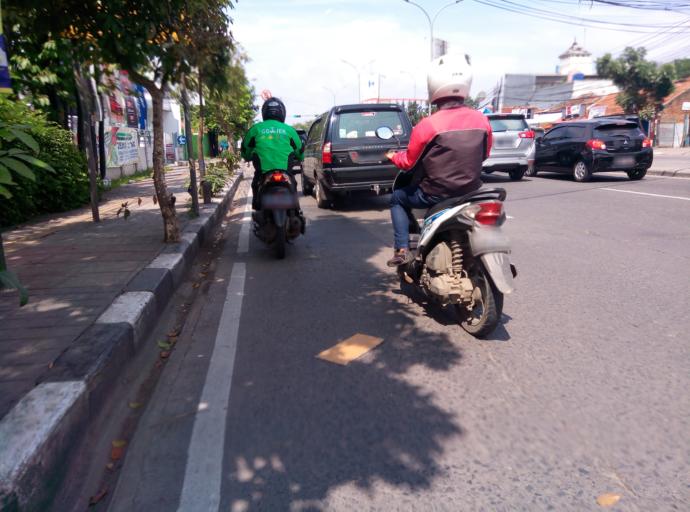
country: ID
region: West Java
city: Bandung
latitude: -6.9443
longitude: 107.6421
